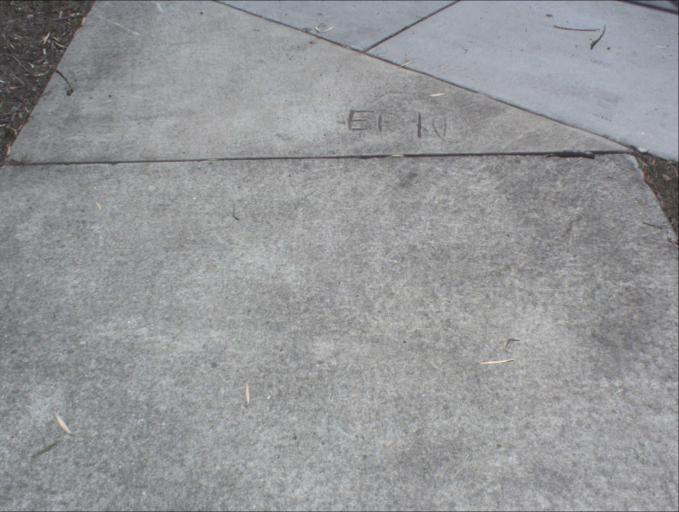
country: AU
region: Queensland
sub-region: Logan
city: Beenleigh
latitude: -27.6996
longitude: 153.2120
